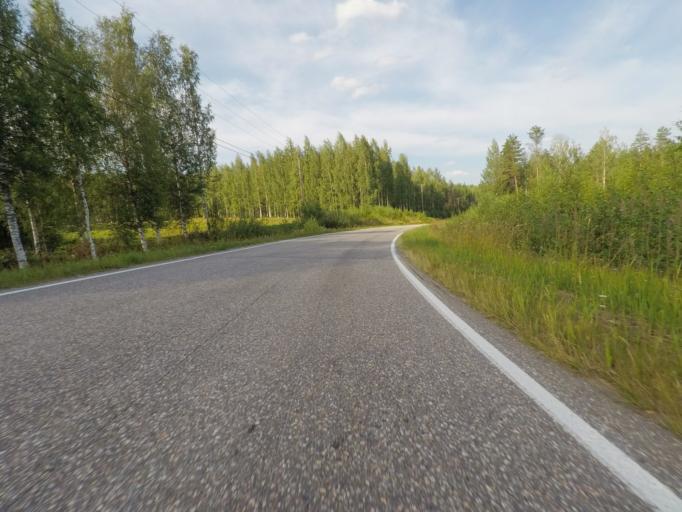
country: FI
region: Southern Savonia
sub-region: Savonlinna
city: Sulkava
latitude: 61.7577
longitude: 28.2272
